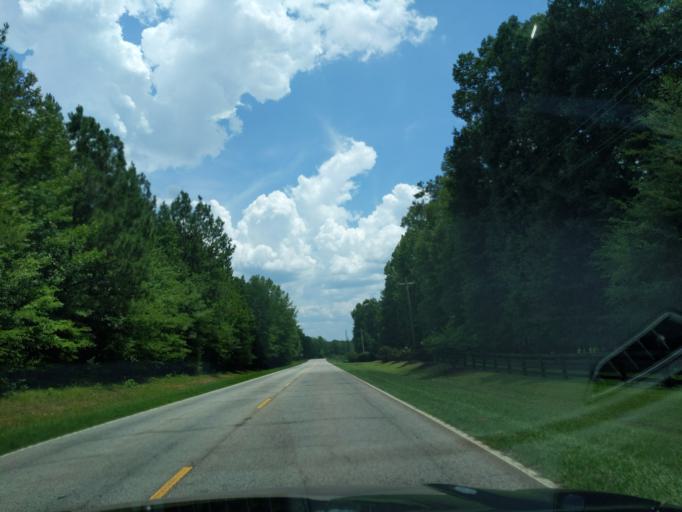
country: US
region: South Carolina
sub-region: Edgefield County
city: Edgefield
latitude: 33.8680
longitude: -81.9917
